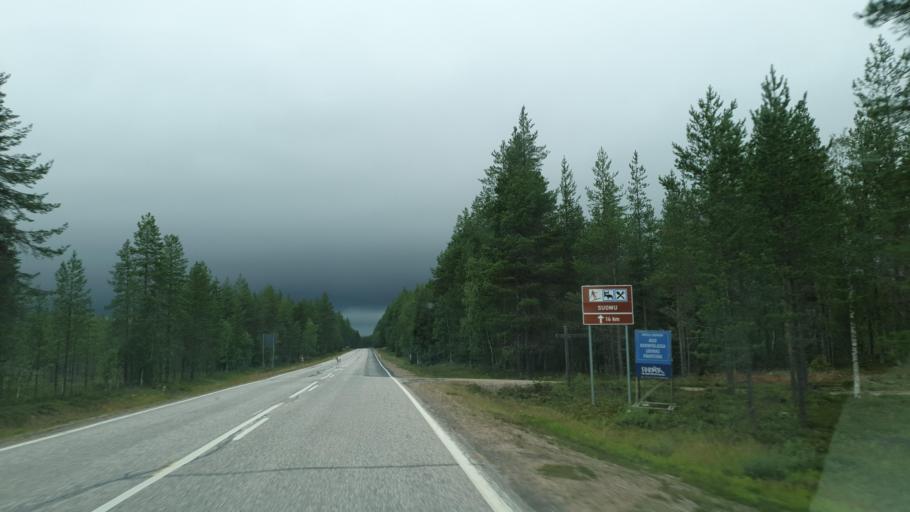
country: FI
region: Lapland
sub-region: Itae-Lappi
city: Posio
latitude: 66.5122
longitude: 28.3196
